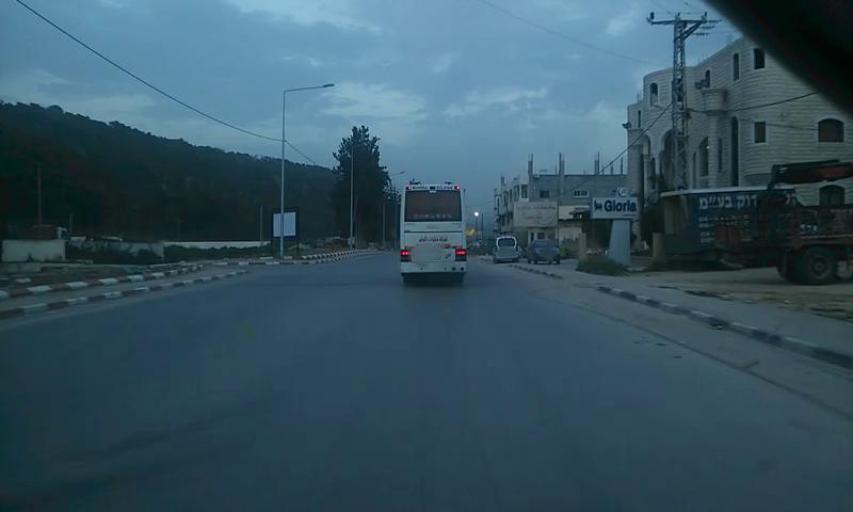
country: PS
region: West Bank
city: Iktabah
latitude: 32.3192
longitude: 35.0637
